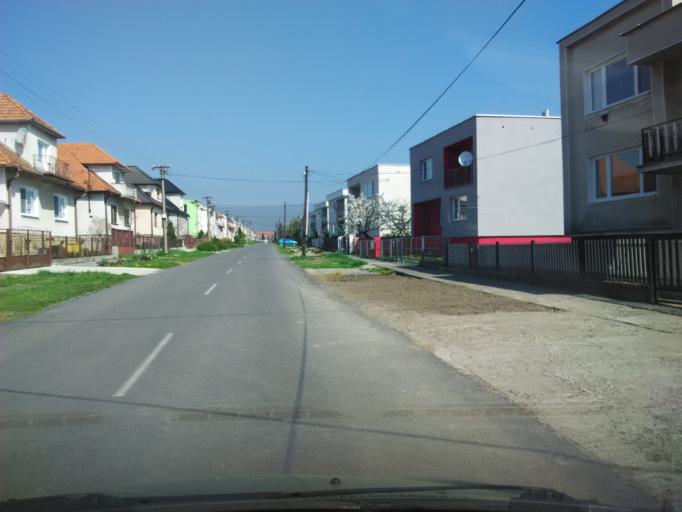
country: SK
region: Nitriansky
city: Tlmace
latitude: 48.2871
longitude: 18.5972
